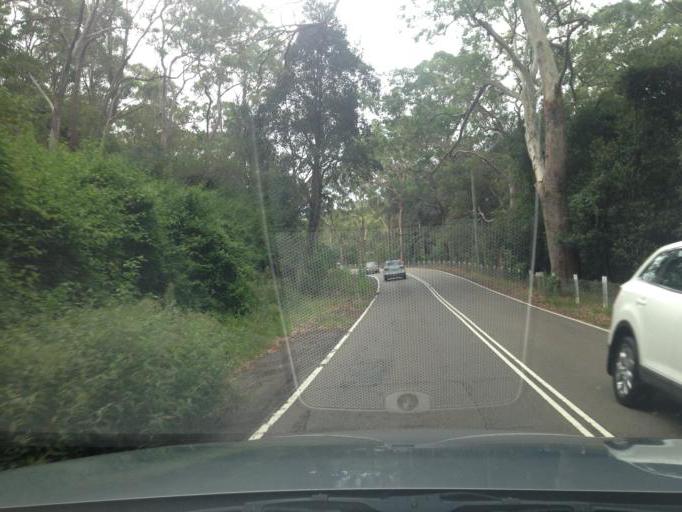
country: AU
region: New South Wales
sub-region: Ku-ring-gai
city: Lindfield
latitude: -33.7854
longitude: 151.1550
